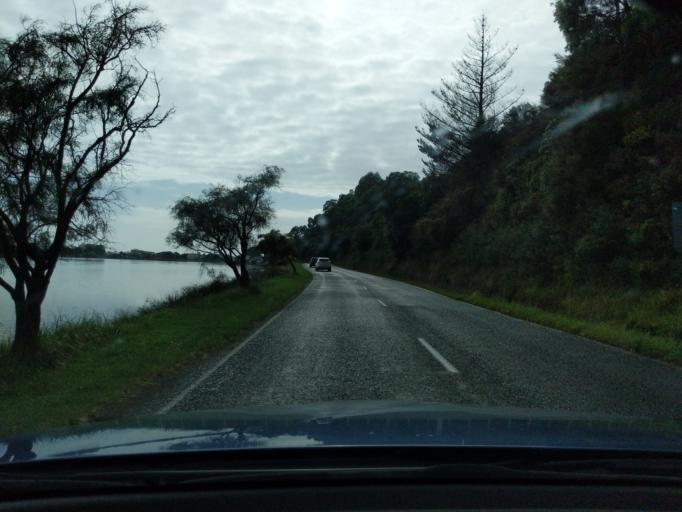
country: NZ
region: Tasman
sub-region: Tasman District
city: Takaka
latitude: -40.6807
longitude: 172.6755
